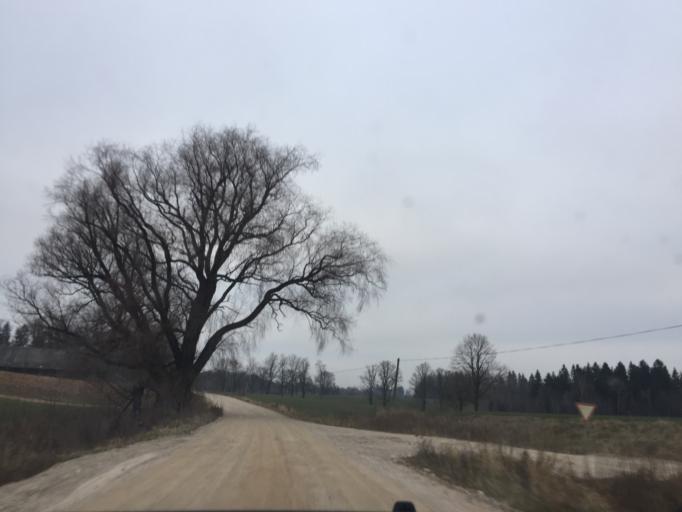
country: LV
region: Raunas
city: Rauna
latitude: 57.3199
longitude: 25.5978
